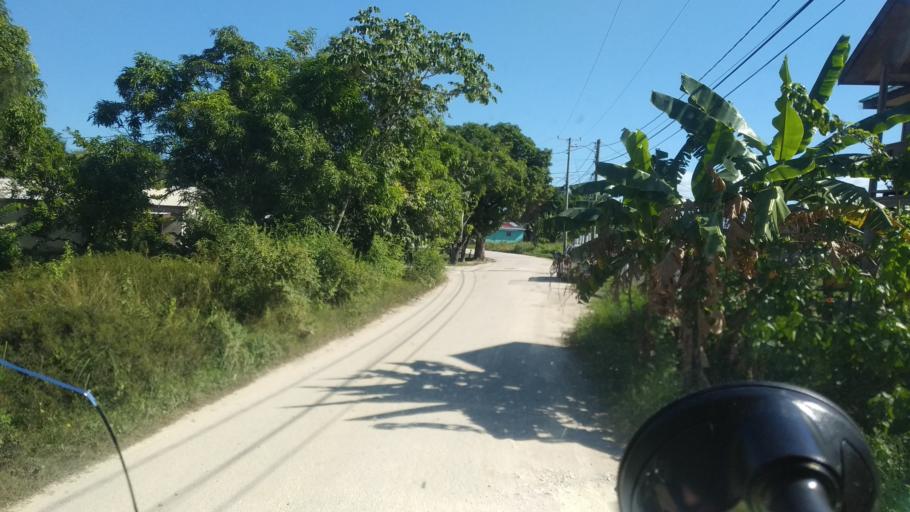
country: BZ
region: Belize
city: Belize City
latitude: 17.5555
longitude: -88.3046
